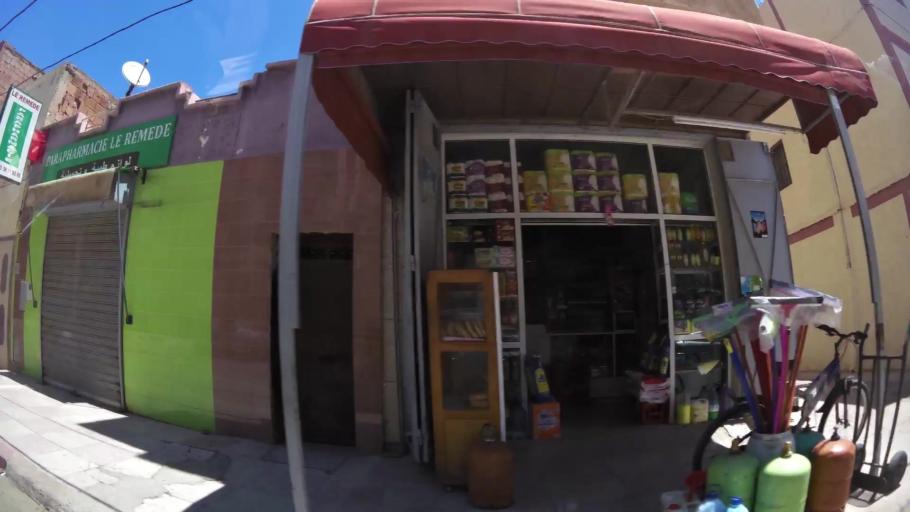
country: MA
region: Oriental
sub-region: Oujda-Angad
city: Oujda
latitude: 34.6661
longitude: -1.9360
